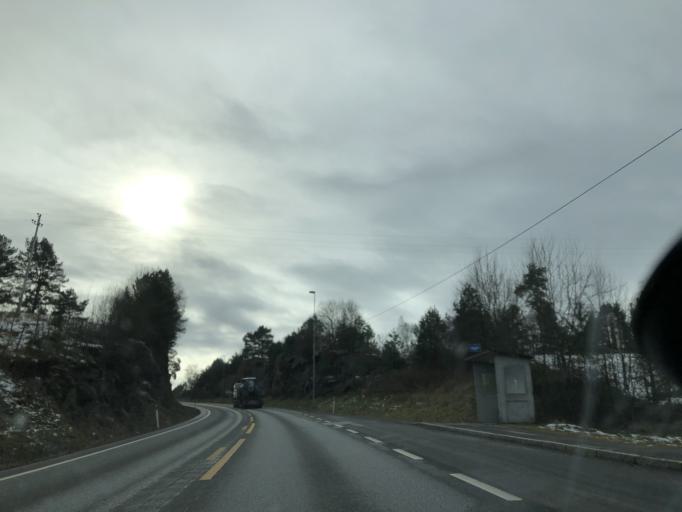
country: NO
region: Rogaland
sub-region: Tysvaer
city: Aksdal
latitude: 59.4775
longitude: 5.5284
